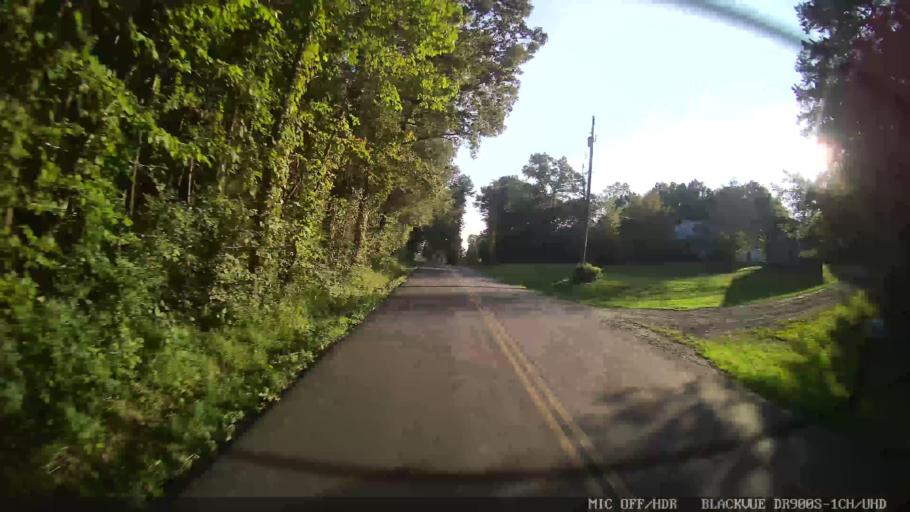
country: US
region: Tennessee
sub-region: Bradley County
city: Wildwood Lake
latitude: 35.0127
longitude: -84.7838
